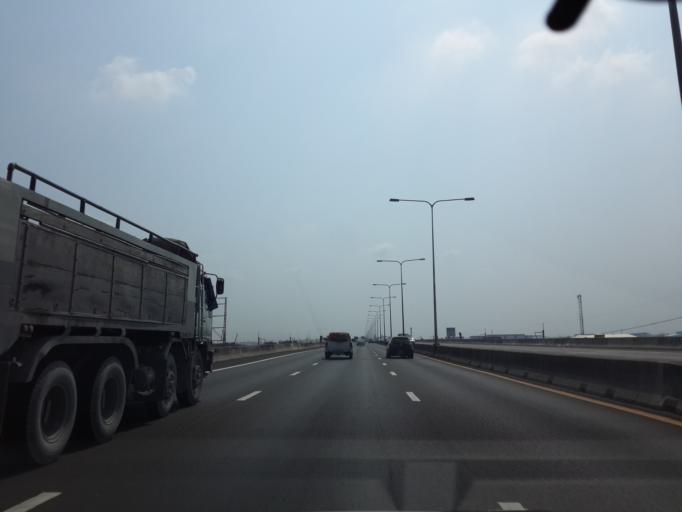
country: TH
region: Samut Prakan
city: Bang Bo District
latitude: 13.6037
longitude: 100.7803
